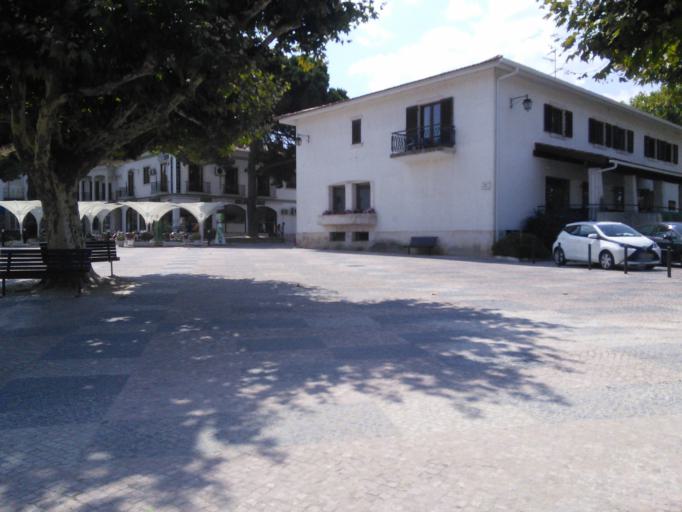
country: PT
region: Leiria
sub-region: Batalha
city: Batalha
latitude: 39.6579
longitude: -8.8260
